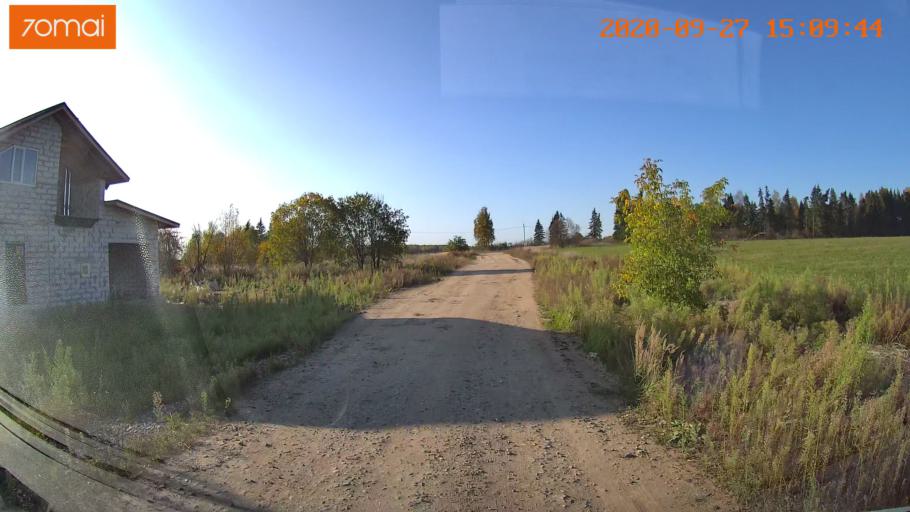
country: RU
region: Ivanovo
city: Furmanov
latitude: 57.1647
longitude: 41.0730
